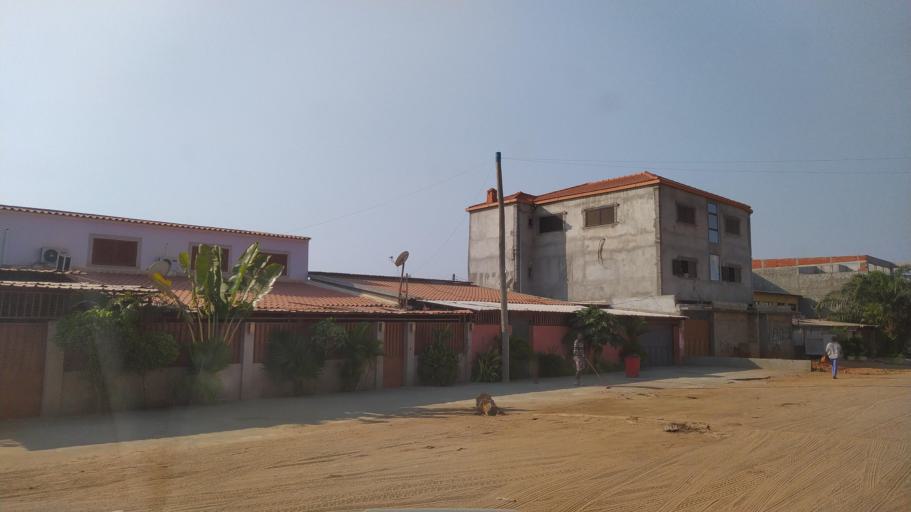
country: AO
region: Luanda
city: Luanda
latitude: -8.9348
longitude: 13.2555
